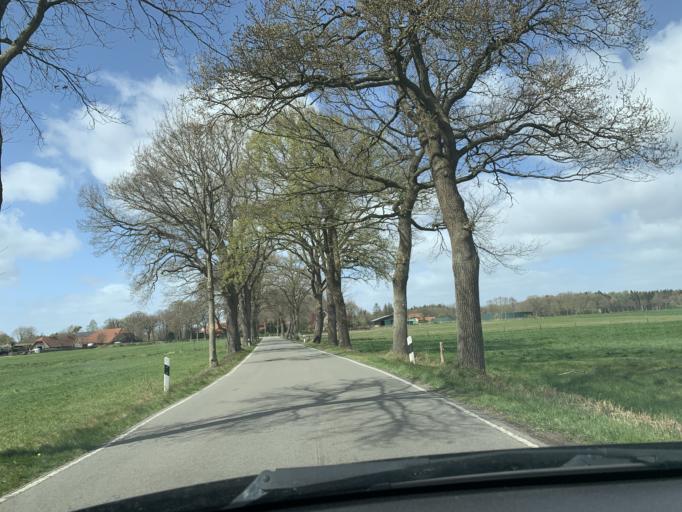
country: DE
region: Lower Saxony
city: Westerstede
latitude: 53.3050
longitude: 7.9482
